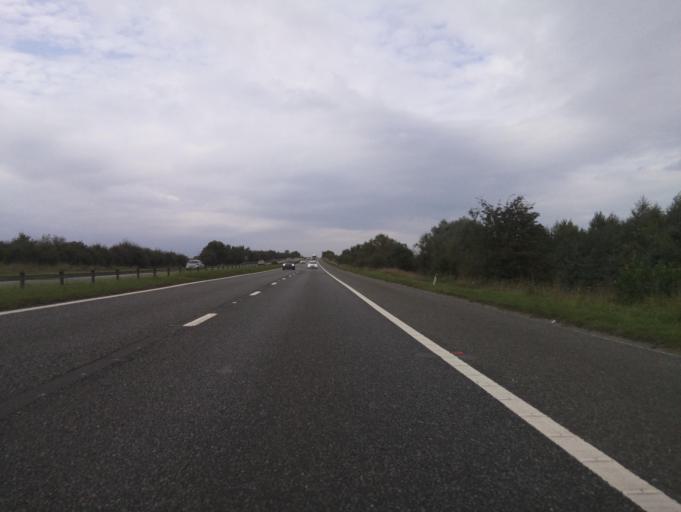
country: GB
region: England
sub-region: County Durham
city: Coxhoe
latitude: 54.7434
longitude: -1.5161
